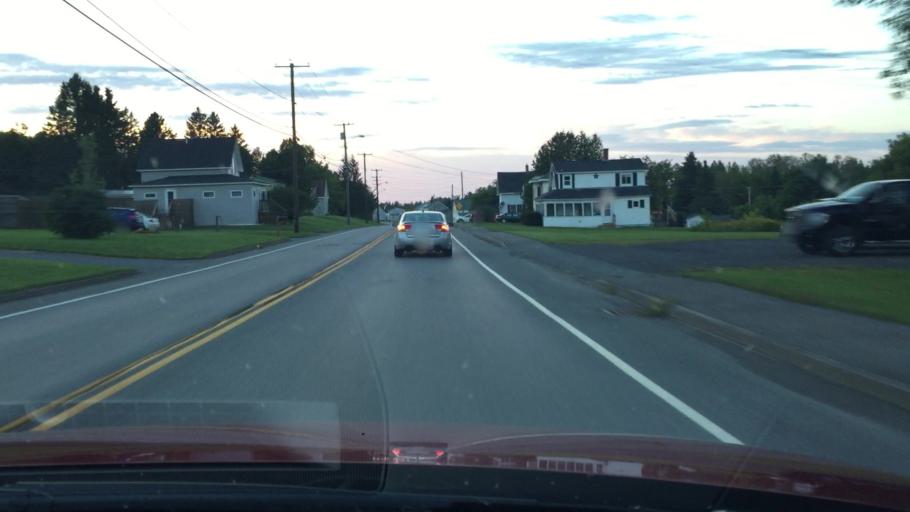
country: US
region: Maine
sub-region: Aroostook County
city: Easton
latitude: 46.5202
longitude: -67.8717
